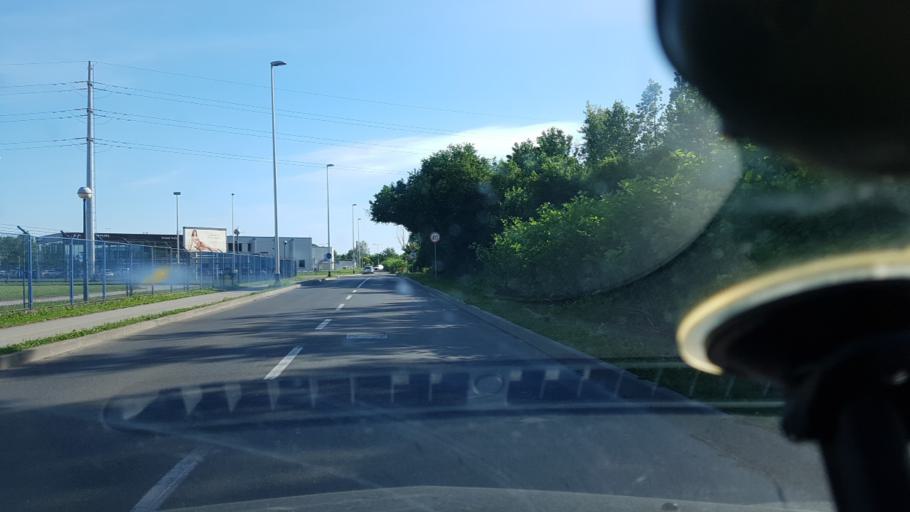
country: HR
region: Grad Zagreb
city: Stenjevec
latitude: 45.8001
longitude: 15.8727
